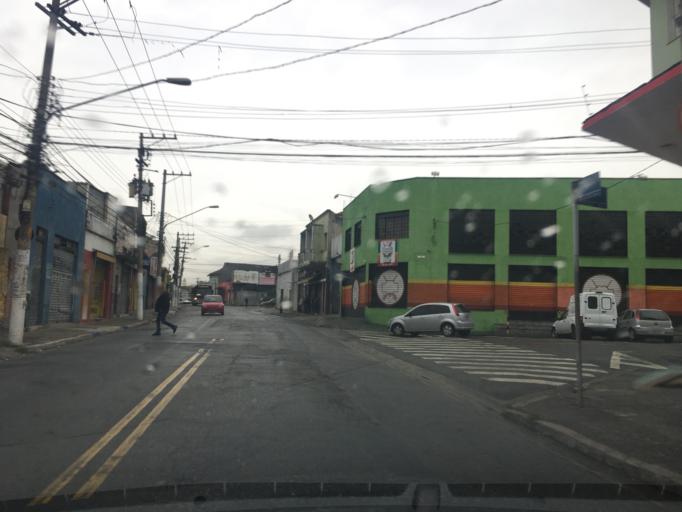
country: BR
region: Sao Paulo
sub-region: Guarulhos
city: Guarulhos
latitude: -23.5118
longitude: -46.5510
